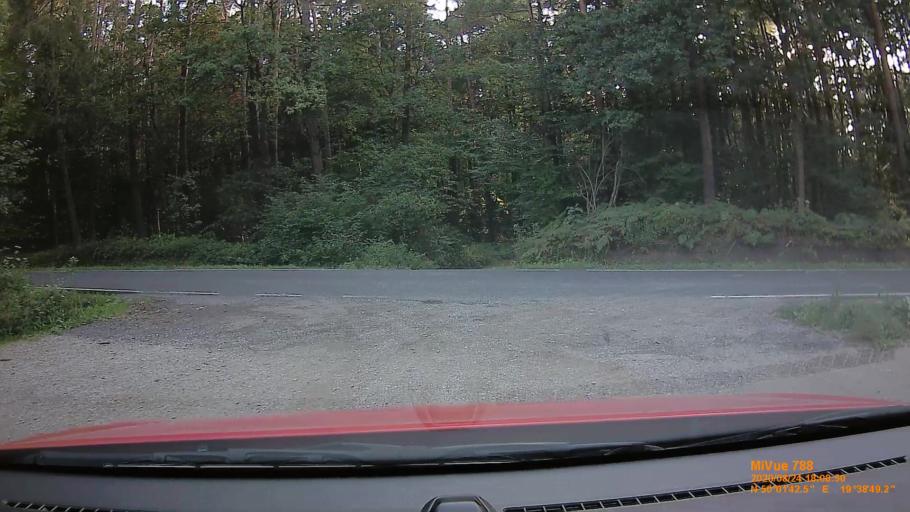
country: PL
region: Lesser Poland Voivodeship
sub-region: Powiat krakowski
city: Sanka
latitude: 50.0285
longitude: 19.6470
